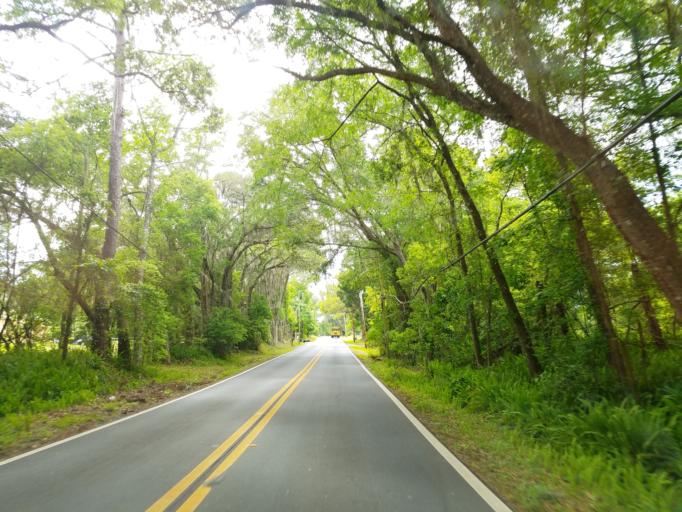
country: US
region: Florida
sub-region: Hernando County
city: Brooksville
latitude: 28.5563
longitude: -82.3692
